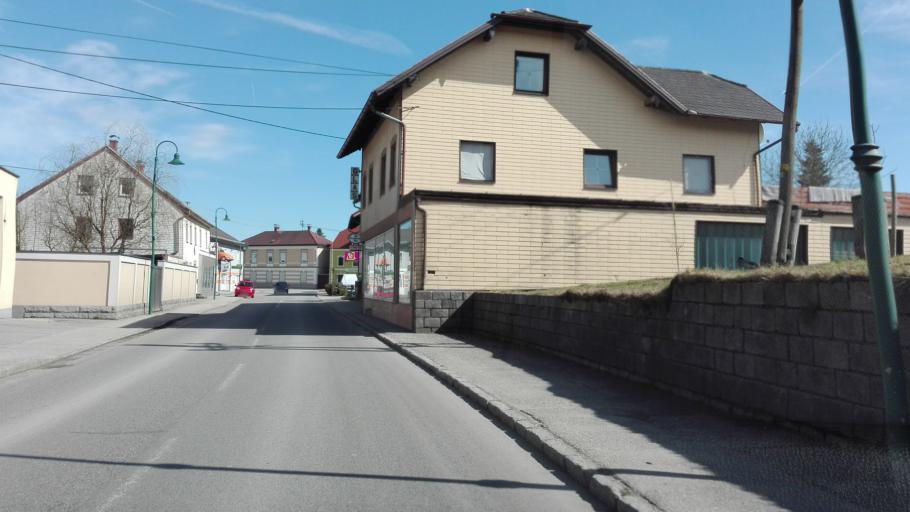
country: AT
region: Upper Austria
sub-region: Politischer Bezirk Scharding
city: Sankt Marienkirchen bei Schaerding
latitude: 48.3517
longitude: 13.6432
